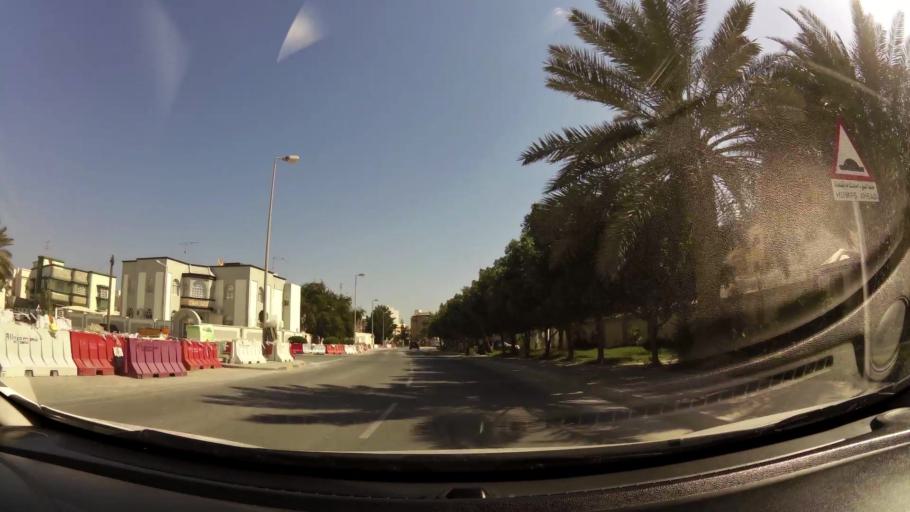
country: BH
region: Manama
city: Manama
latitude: 26.2083
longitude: 50.5803
